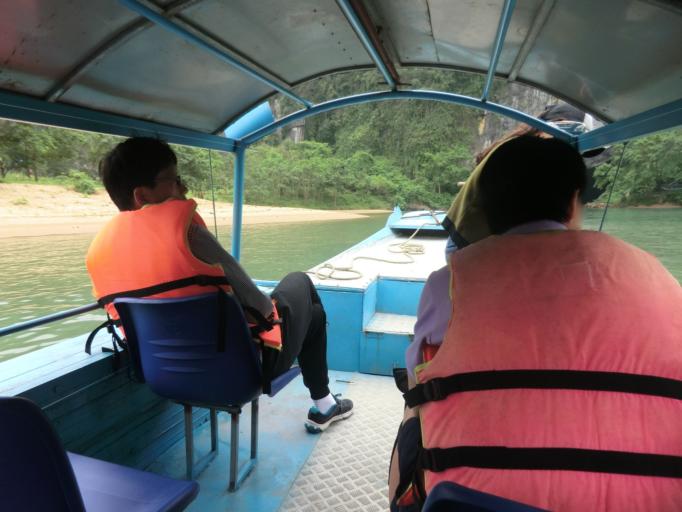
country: VN
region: Quang Binh
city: Ba Don
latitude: 17.5828
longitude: 106.2823
